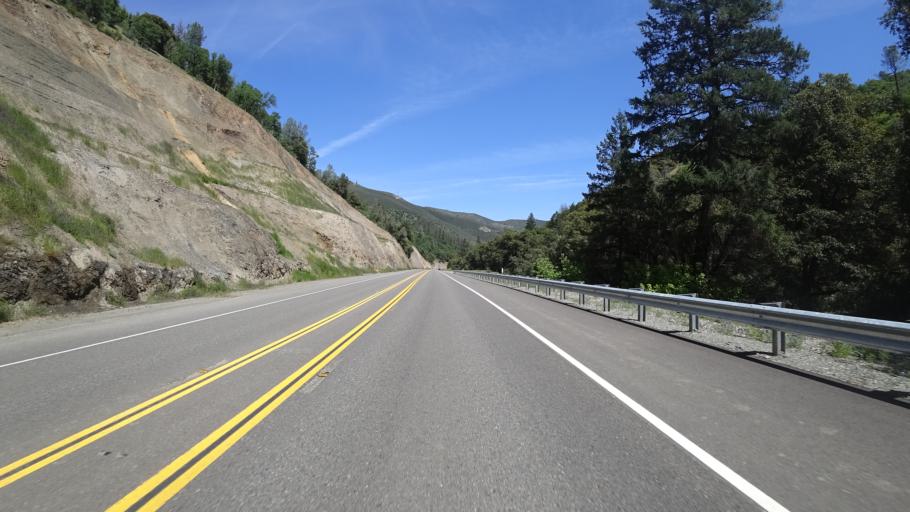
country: US
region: California
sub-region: Trinity County
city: Lewiston
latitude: 40.6706
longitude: -122.6826
